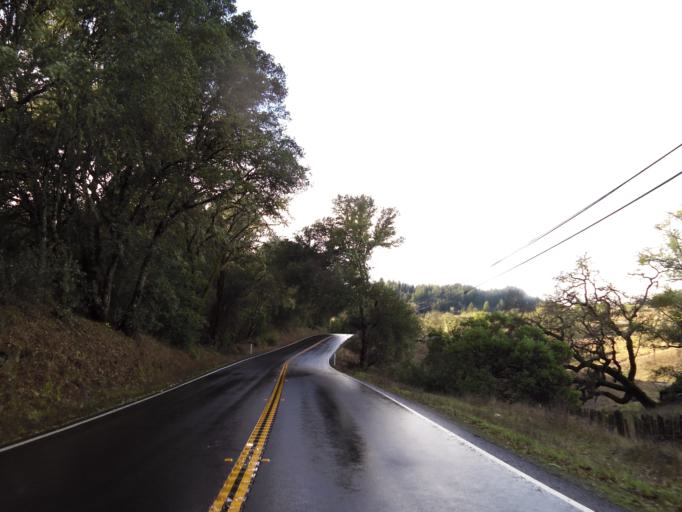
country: US
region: California
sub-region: Sonoma County
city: Cloverdale
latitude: 38.8761
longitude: -123.1074
